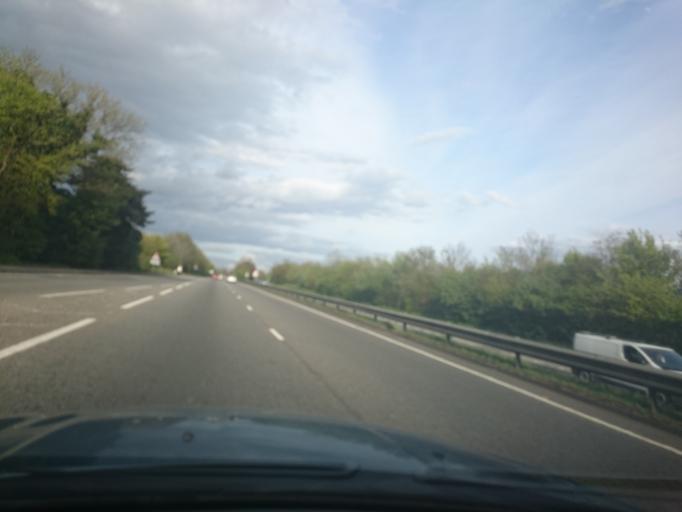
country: GB
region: England
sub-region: Surrey
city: Seale
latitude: 51.2263
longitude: -0.7199
